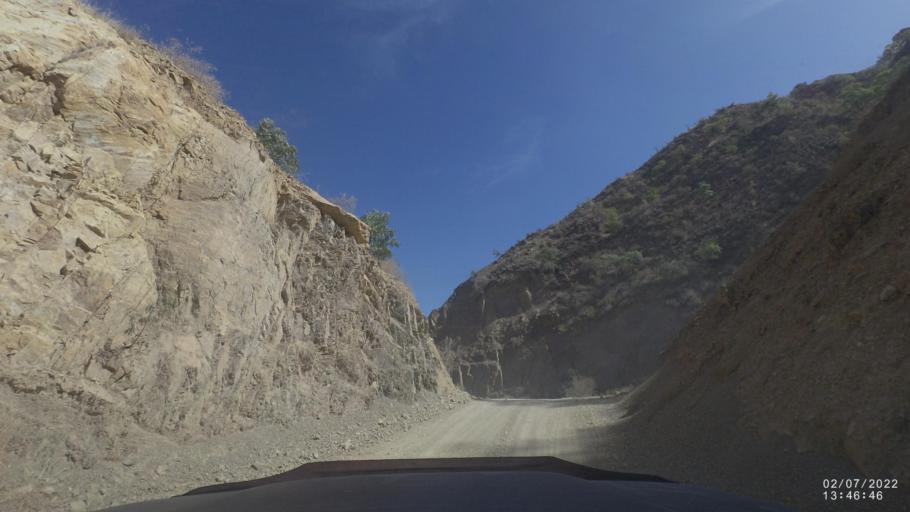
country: BO
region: Cochabamba
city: Irpa Irpa
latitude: -17.8151
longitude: -66.3675
